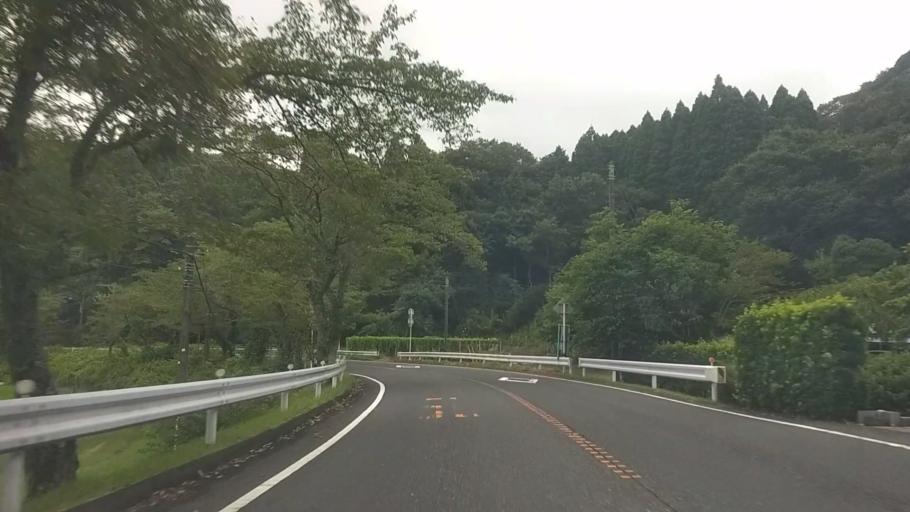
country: JP
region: Chiba
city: Kawaguchi
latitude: 35.2421
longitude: 140.0717
